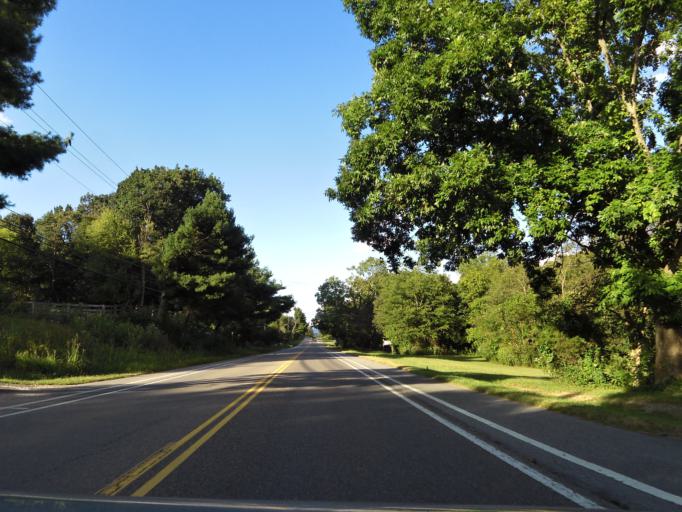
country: US
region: Tennessee
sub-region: Grainger County
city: Blaine
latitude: 36.1634
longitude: -83.6968
